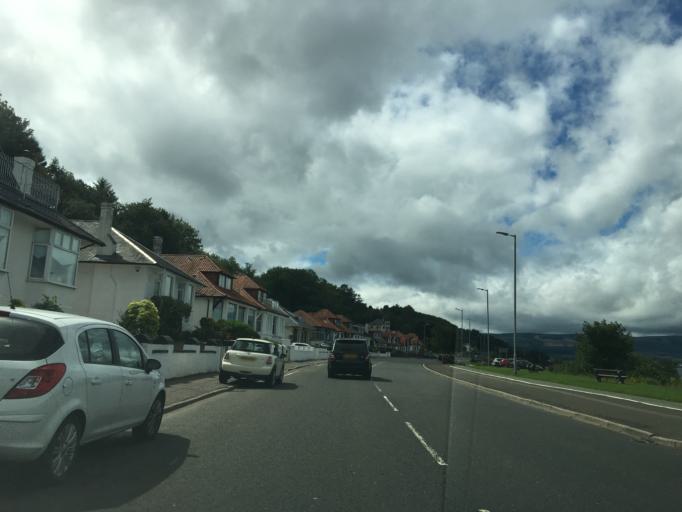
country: GB
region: Scotland
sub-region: Inverclyde
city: Gourock
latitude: 55.9537
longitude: -4.8388
